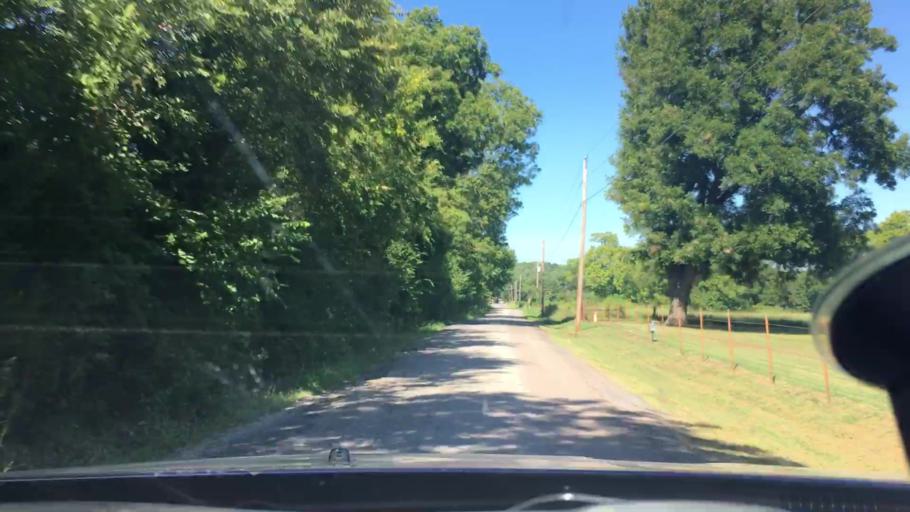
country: US
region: Oklahoma
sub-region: Pontotoc County
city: Ada
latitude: 34.7237
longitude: -96.6638
